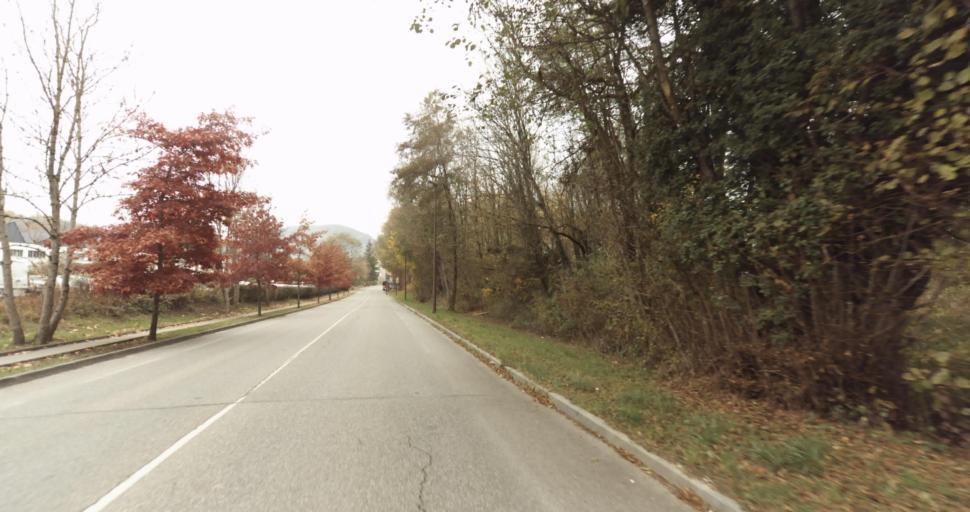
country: FR
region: Rhone-Alpes
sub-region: Departement de la Haute-Savoie
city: Poisy
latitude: 45.9287
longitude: 6.0624
